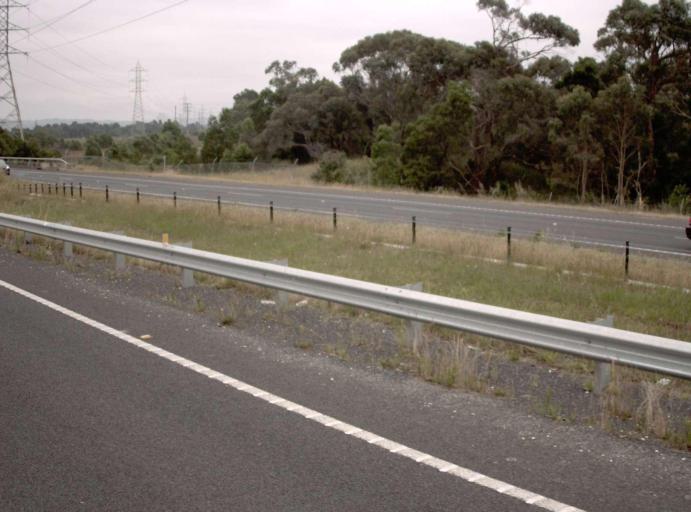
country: AU
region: Victoria
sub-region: Latrobe
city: Morwell
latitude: -38.2410
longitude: 146.3859
